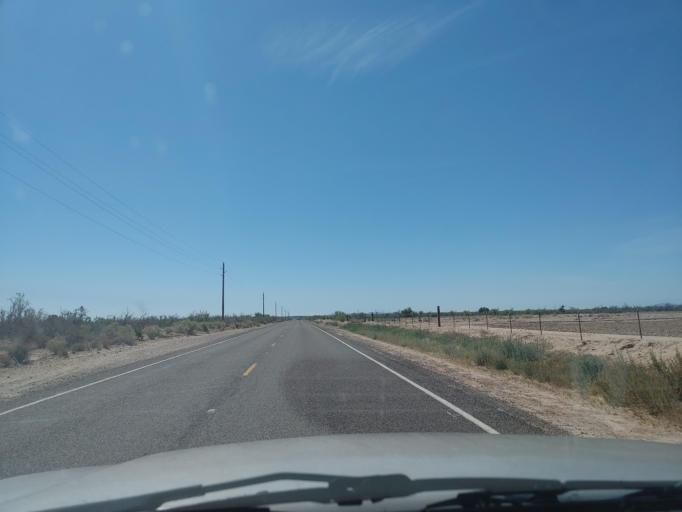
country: US
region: Arizona
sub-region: Maricopa County
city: Gila Bend
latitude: 32.9781
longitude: -113.3060
